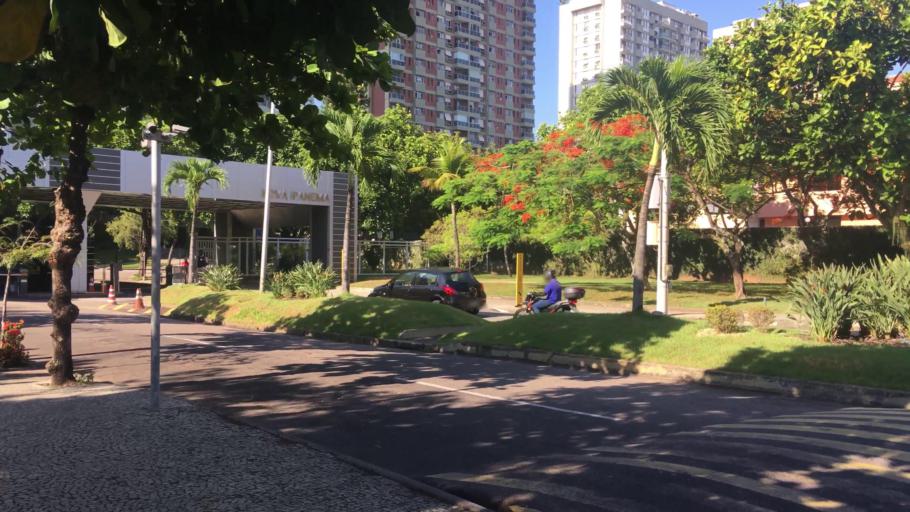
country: BR
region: Rio de Janeiro
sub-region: Rio De Janeiro
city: Rio de Janeiro
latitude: -23.0005
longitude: -43.3607
